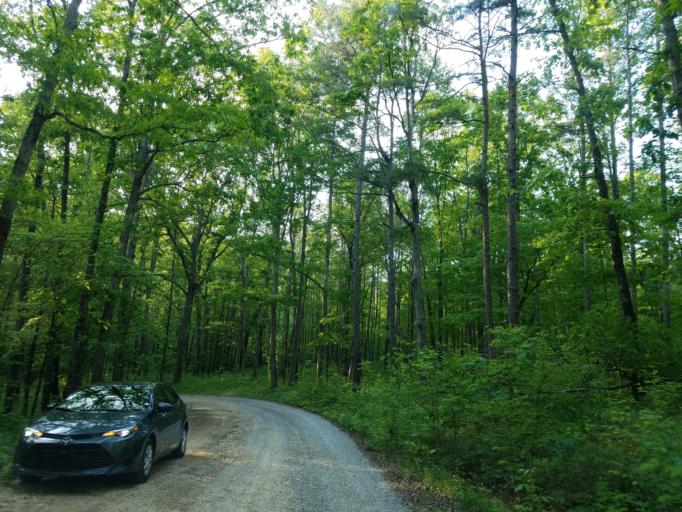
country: US
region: Georgia
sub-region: Gordon County
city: Calhoun
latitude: 34.6145
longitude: -85.0862
